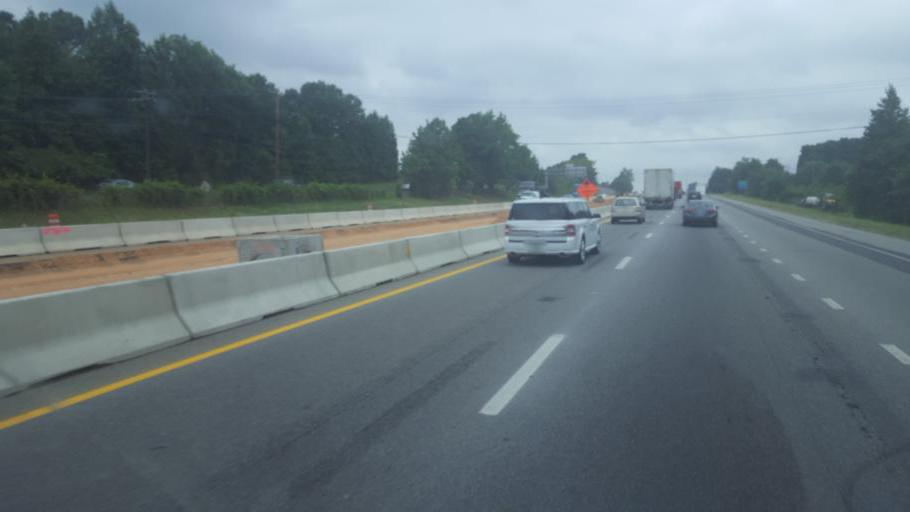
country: US
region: North Carolina
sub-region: Gaston County
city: Davidson
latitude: 35.5458
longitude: -80.8588
